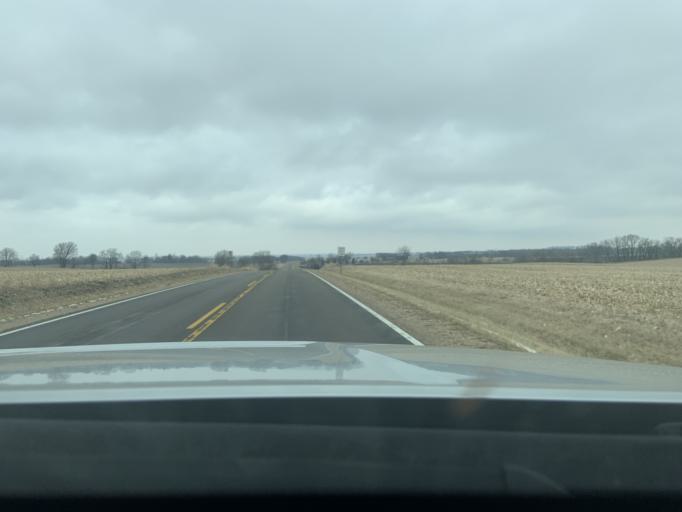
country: US
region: Illinois
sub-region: LaSalle County
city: Sheridan
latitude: 41.4757
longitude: -88.6159
